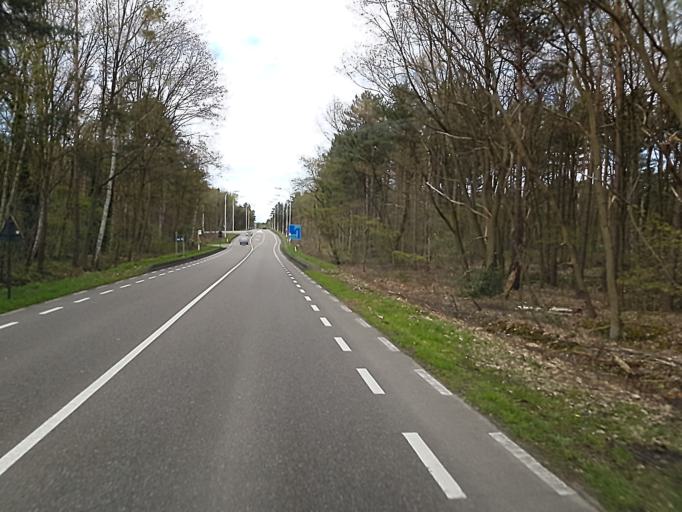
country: BE
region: Flanders
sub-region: Provincie Limburg
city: Zutendaal
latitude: 50.9725
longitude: 5.5524
